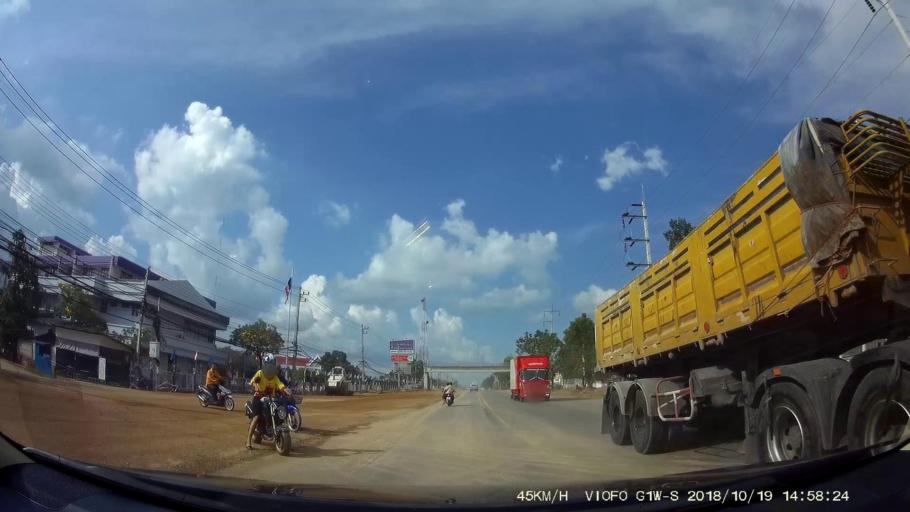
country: TH
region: Chaiyaphum
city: Phu Khiao
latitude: 16.3746
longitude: 102.1293
